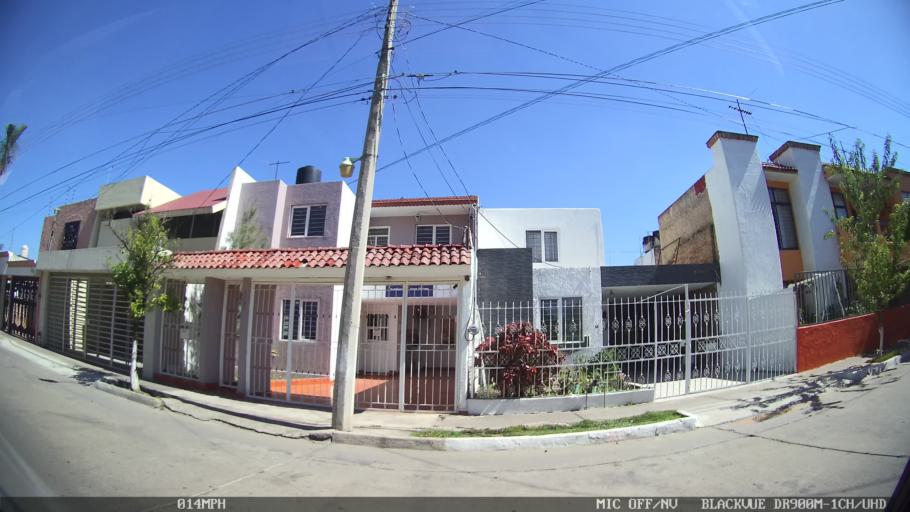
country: MX
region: Jalisco
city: Tlaquepaque
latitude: 20.6452
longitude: -103.2918
